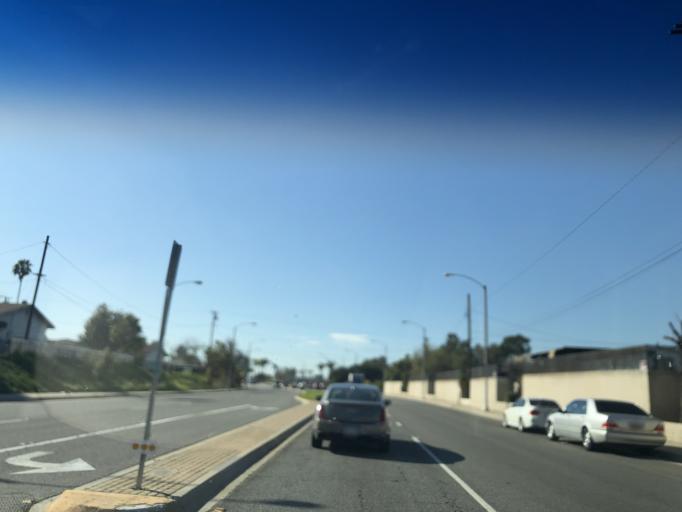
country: US
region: California
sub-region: Los Angeles County
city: South Whittier
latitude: 33.9366
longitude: -118.0442
